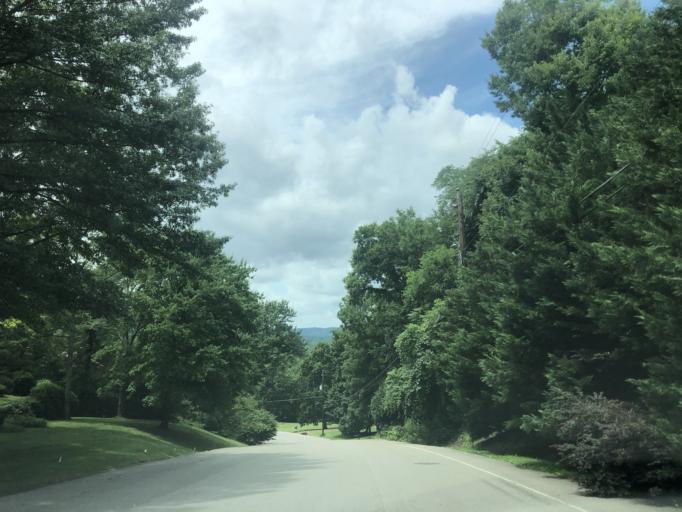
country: US
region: Tennessee
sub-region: Davidson County
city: Forest Hills
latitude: 36.0752
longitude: -86.8273
